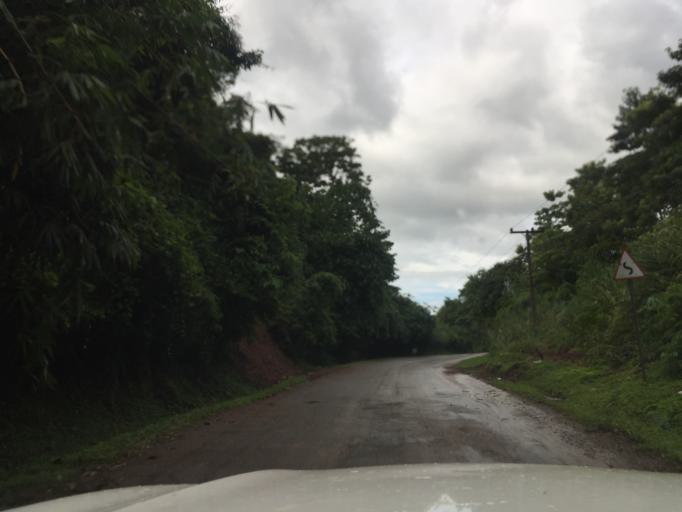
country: LA
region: Oudomxai
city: Muang La
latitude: 20.8018
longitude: 102.0875
